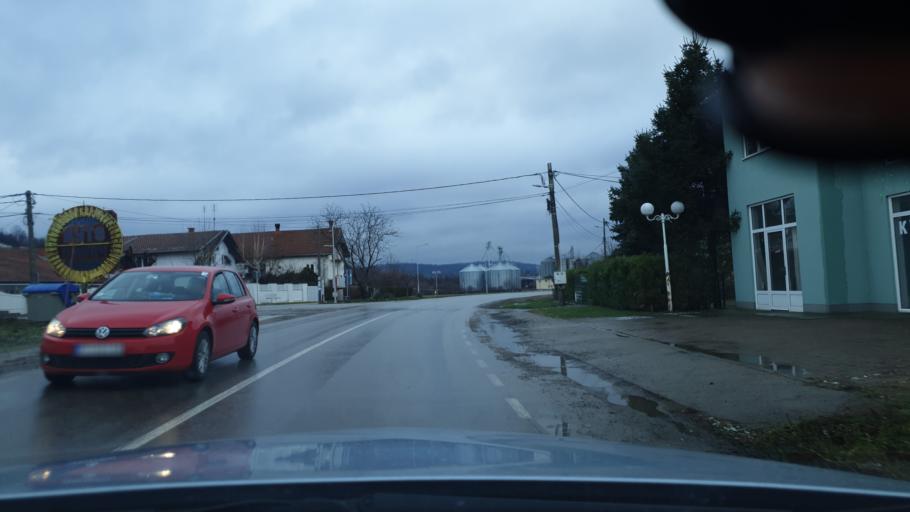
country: RS
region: Central Serbia
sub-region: Branicevski Okrug
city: Petrovac
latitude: 44.4036
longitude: 21.3989
